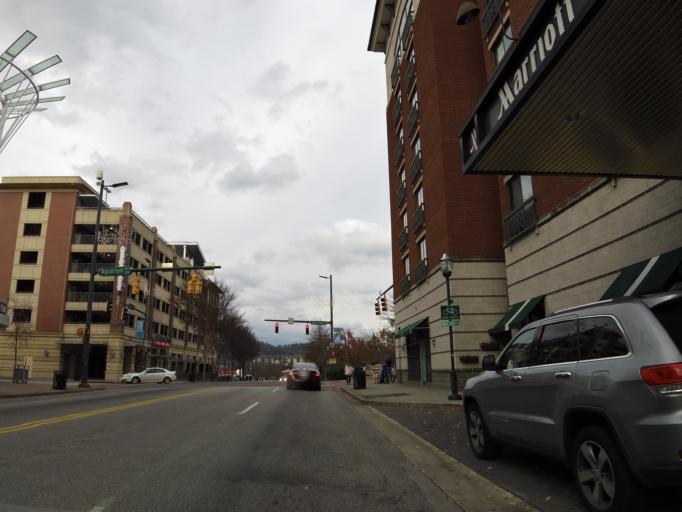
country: US
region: Tennessee
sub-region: Hamilton County
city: Chattanooga
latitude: 35.0544
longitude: -85.3119
